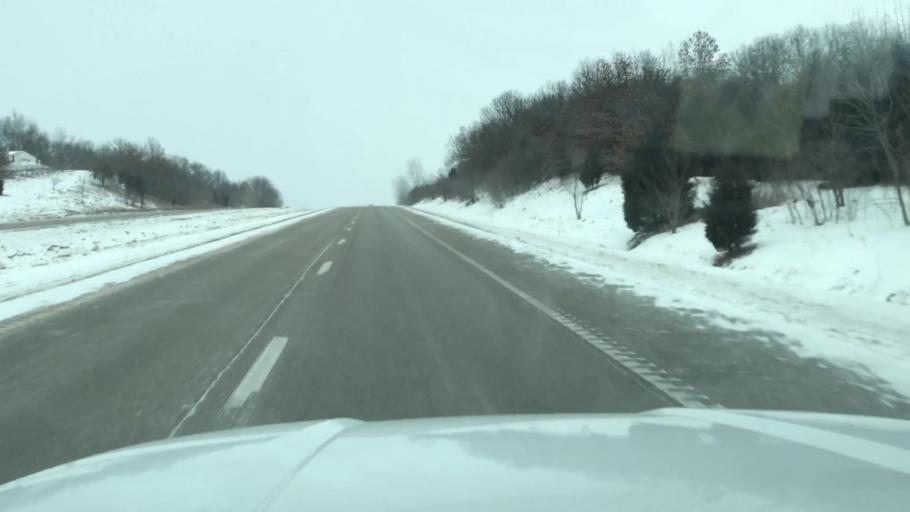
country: US
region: Missouri
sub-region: Clinton County
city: Gower
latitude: 39.7530
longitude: -94.5899
